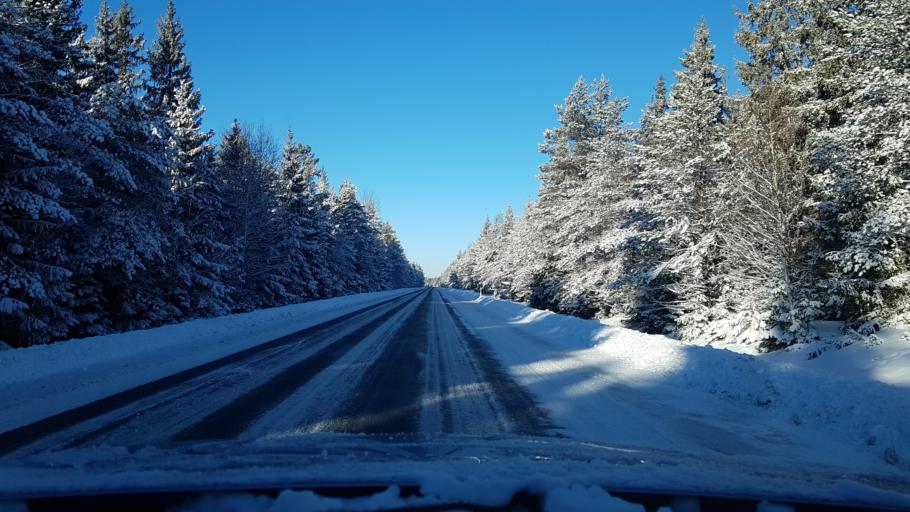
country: EE
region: Hiiumaa
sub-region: Kaerdla linn
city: Kardla
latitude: 58.9838
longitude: 22.8028
